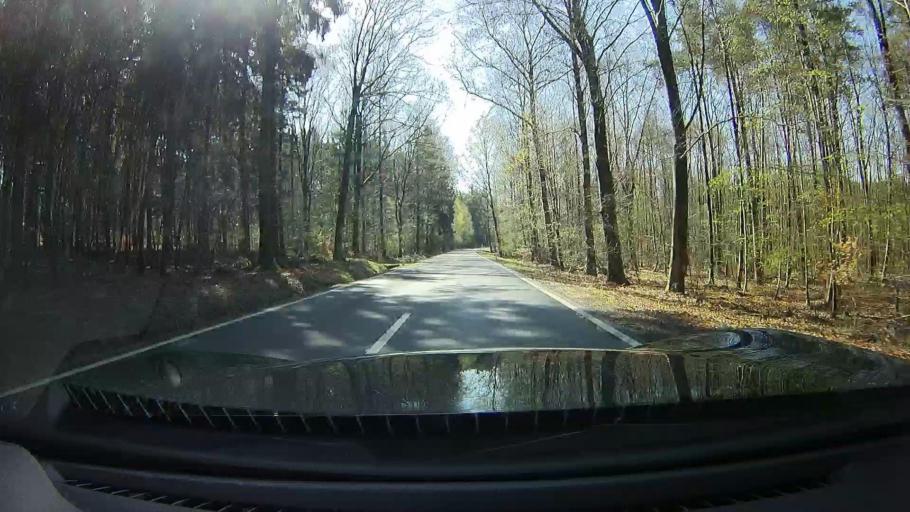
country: DE
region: Baden-Wuerttemberg
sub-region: Karlsruhe Region
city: Eberbach
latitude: 49.4229
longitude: 8.9813
